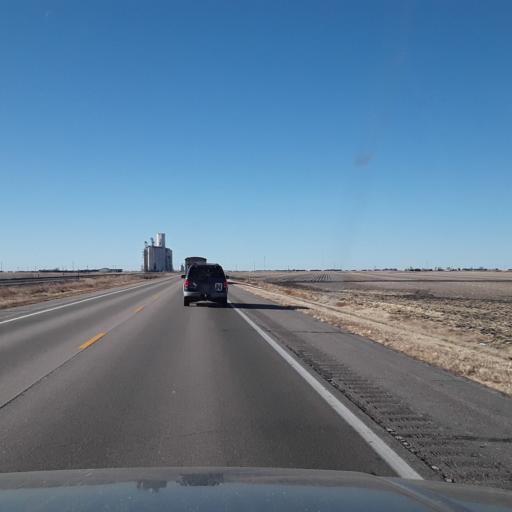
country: US
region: Nebraska
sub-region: Kearney County
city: Minden
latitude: 40.4937
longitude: -99.0157
